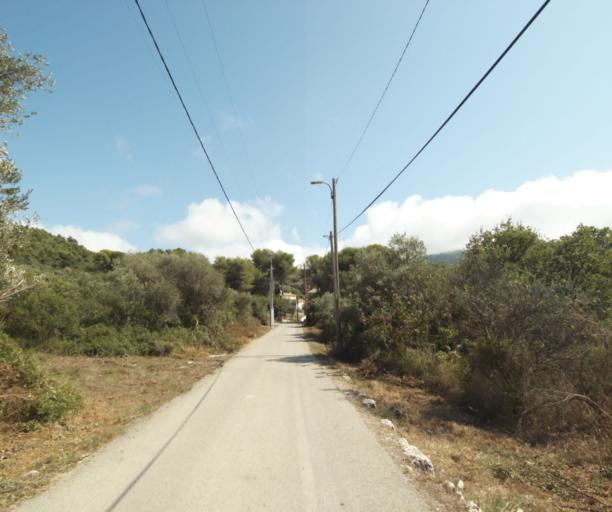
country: FR
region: Provence-Alpes-Cote d'Azur
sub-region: Departement des Alpes-Maritimes
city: Drap
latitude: 43.7552
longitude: 7.3438
